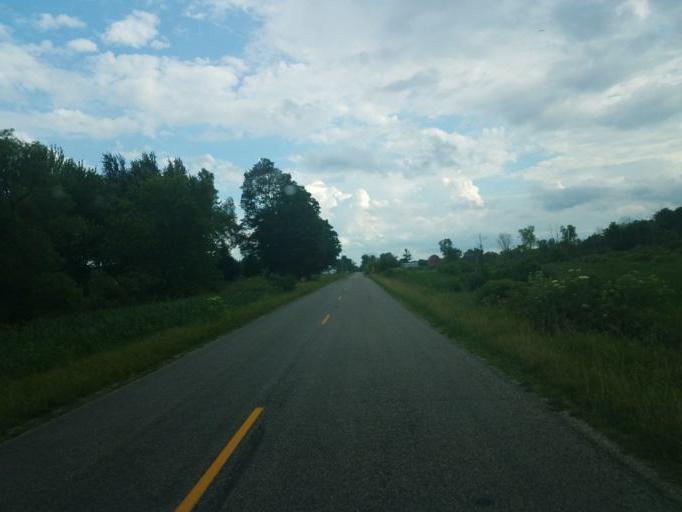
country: US
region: Michigan
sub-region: Eaton County
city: Bellevue
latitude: 42.4615
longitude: -85.0184
